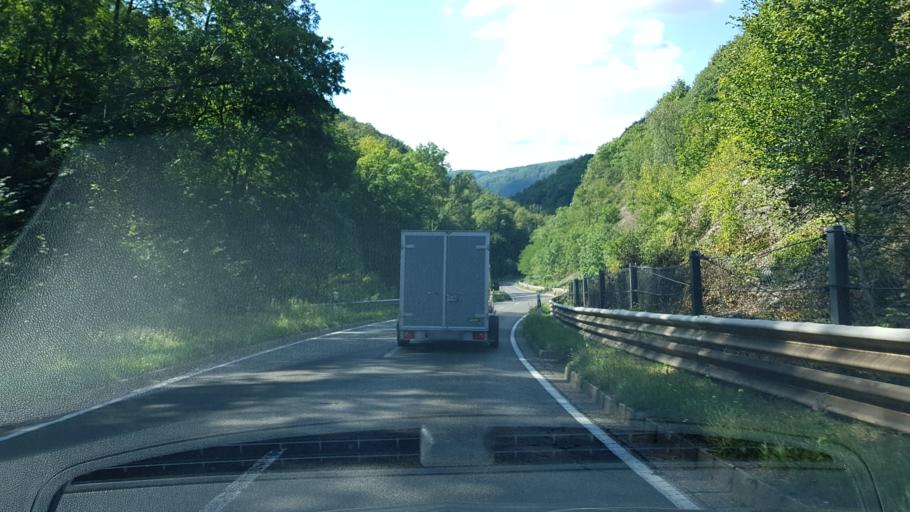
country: DE
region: Rheinland-Pfalz
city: Ernst
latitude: 50.1425
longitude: 7.2518
